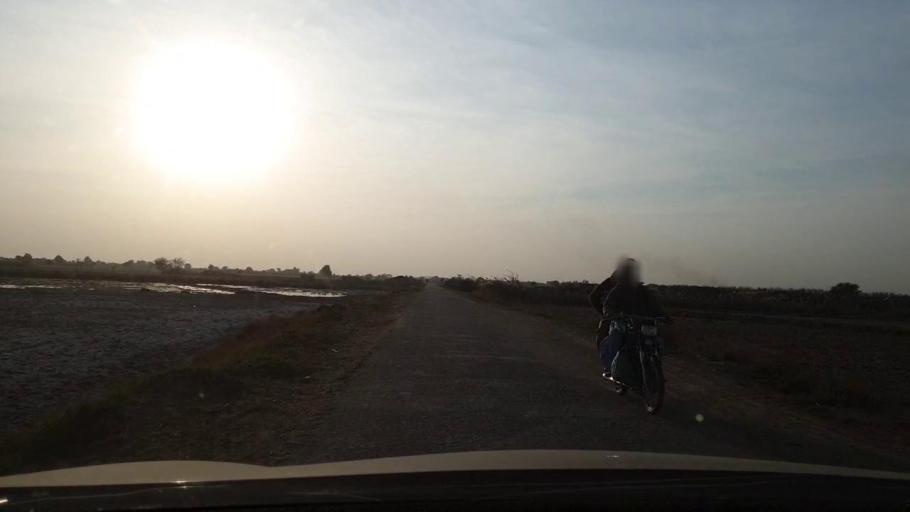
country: PK
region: Sindh
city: Tando Adam
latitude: 25.7089
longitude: 68.7317
